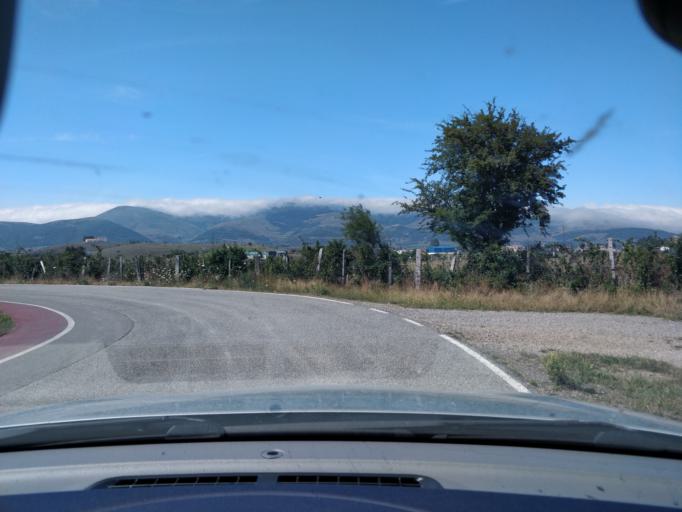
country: ES
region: Cantabria
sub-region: Provincia de Cantabria
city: Reinosa
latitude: 42.9922
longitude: -4.1603
